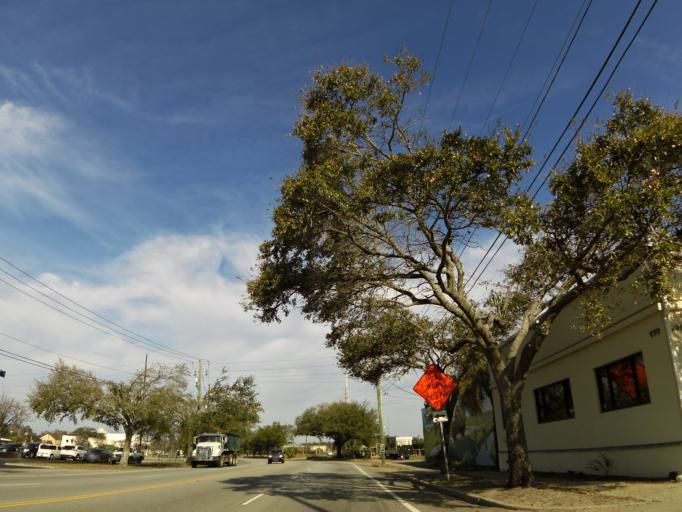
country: US
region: South Carolina
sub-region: Charleston County
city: Charleston
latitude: 32.8069
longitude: -79.9424
